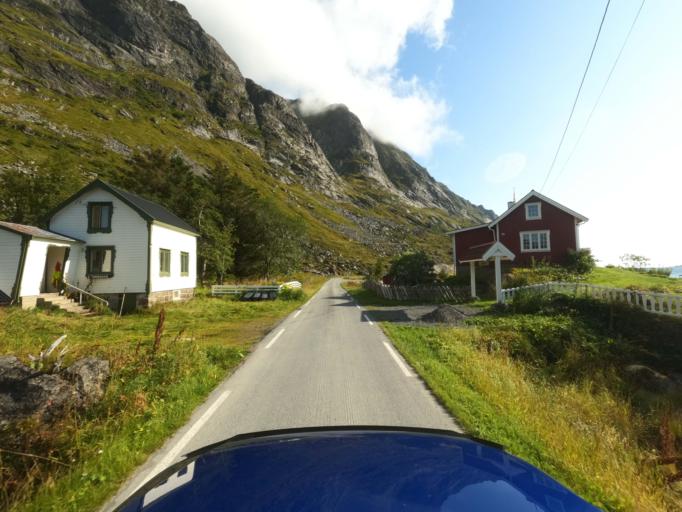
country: NO
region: Nordland
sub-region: Flakstad
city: Ramberg
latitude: 68.0417
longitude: 13.2612
